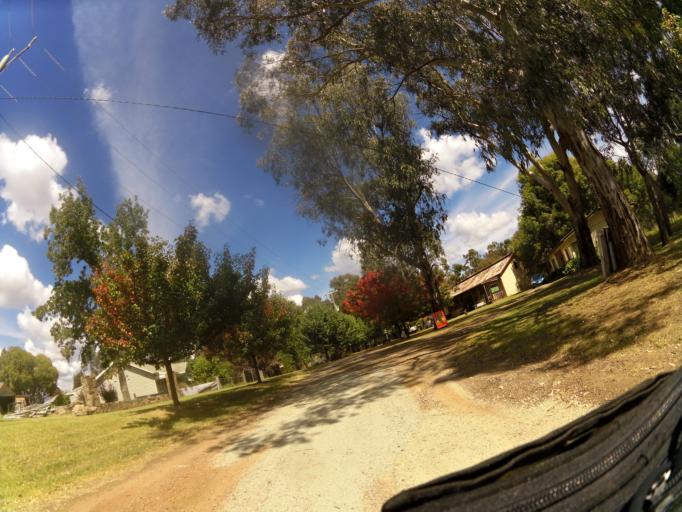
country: AU
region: Victoria
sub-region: Benalla
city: Benalla
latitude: -36.7462
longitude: 146.0122
